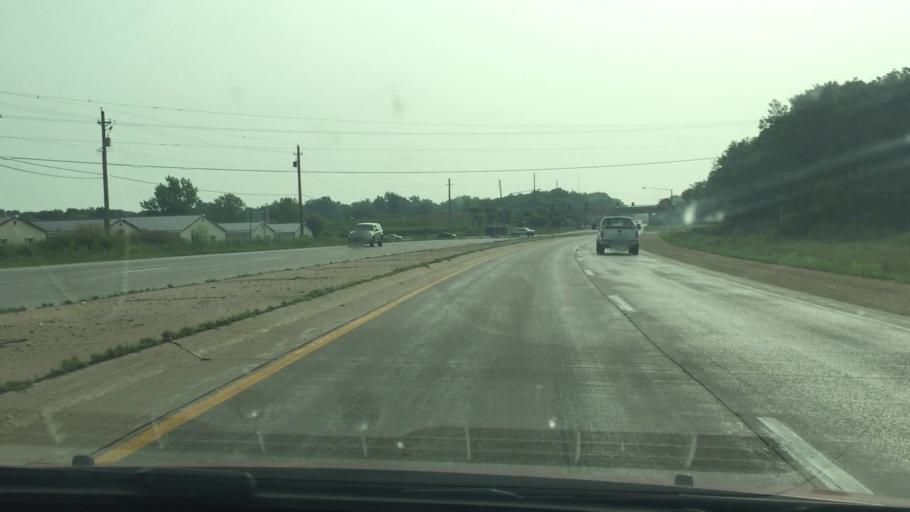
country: US
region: Iowa
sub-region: Scott County
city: Buffalo
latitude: 41.5090
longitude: -90.6768
